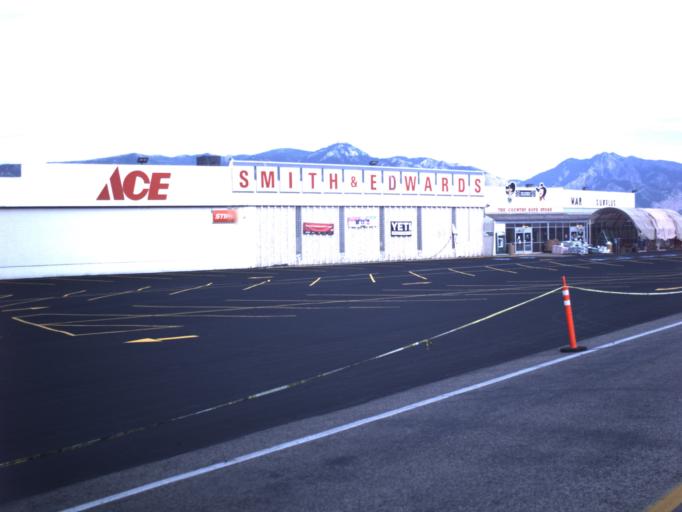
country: US
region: Utah
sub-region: Box Elder County
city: South Willard
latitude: 41.3348
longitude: -112.0368
